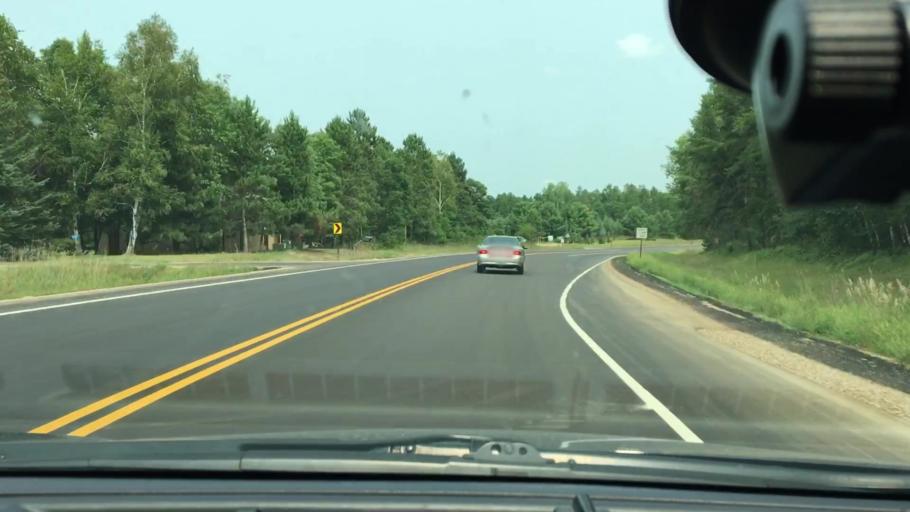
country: US
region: Minnesota
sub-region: Crow Wing County
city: Nisswa
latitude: 46.5277
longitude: -94.2678
